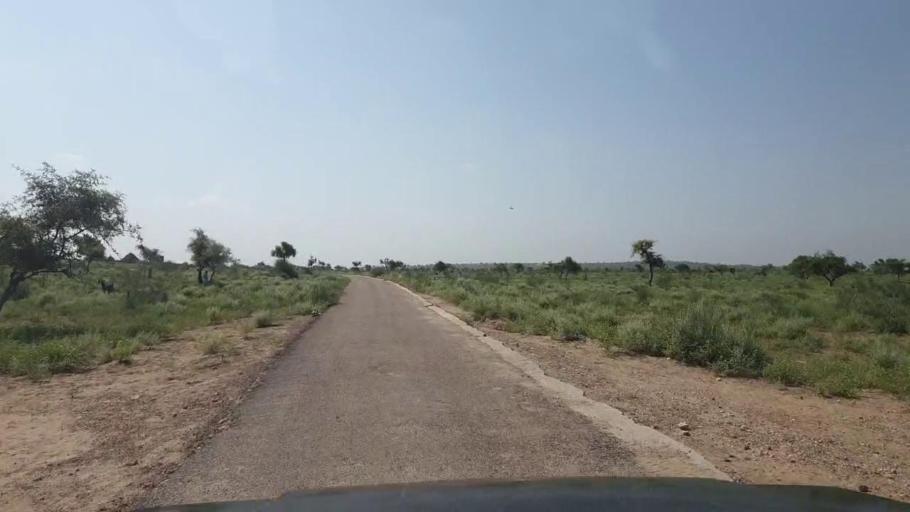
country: PK
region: Sindh
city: Islamkot
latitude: 25.1820
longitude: 70.3926
